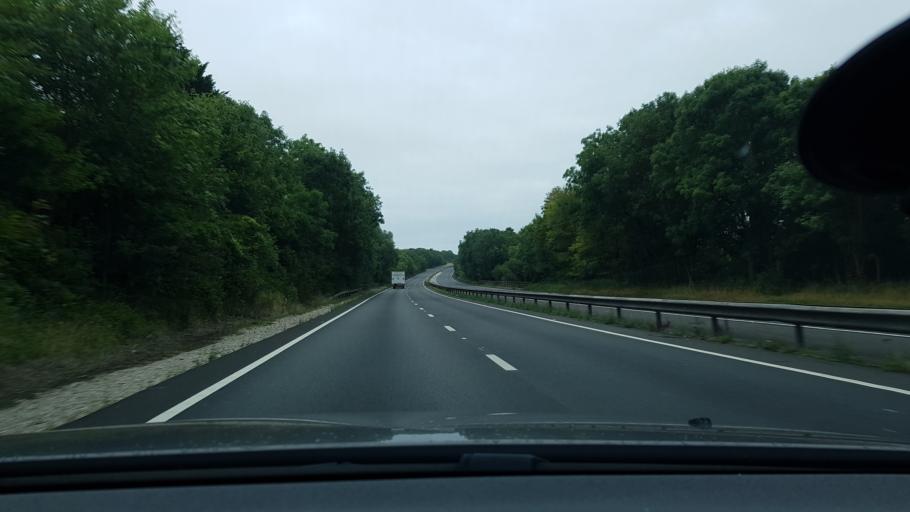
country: GB
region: England
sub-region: Hampshire
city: Overton
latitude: 51.2226
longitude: -1.3438
